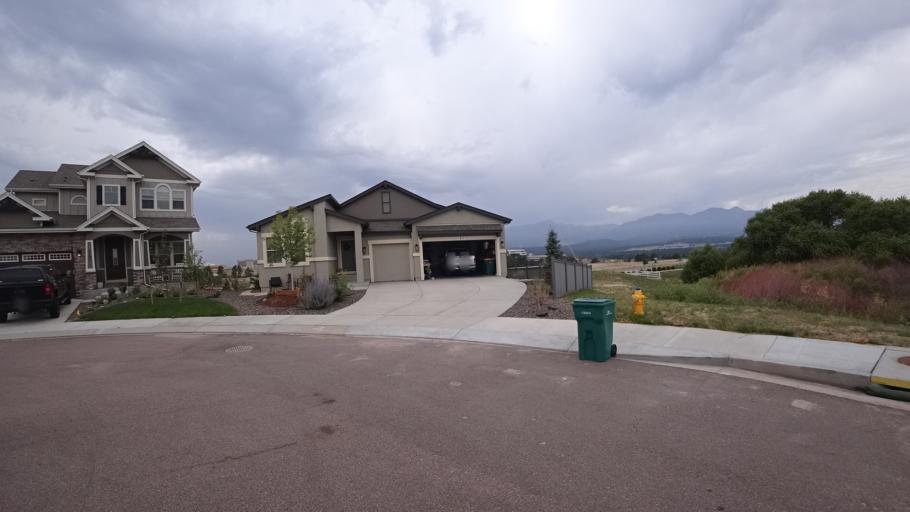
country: US
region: Colorado
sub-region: El Paso County
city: Gleneagle
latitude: 39.0025
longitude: -104.8053
